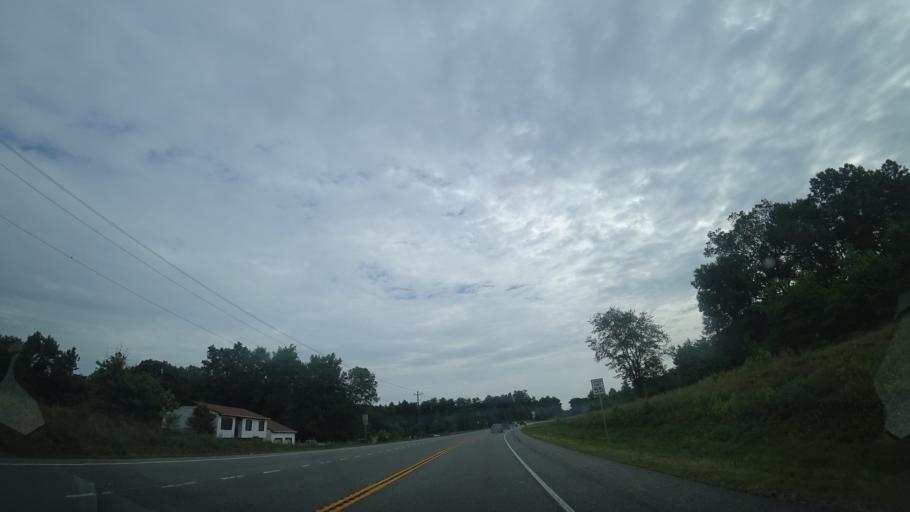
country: US
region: Virginia
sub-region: Spotsylvania County
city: Spotsylvania Courthouse
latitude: 38.1730
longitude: -77.6334
